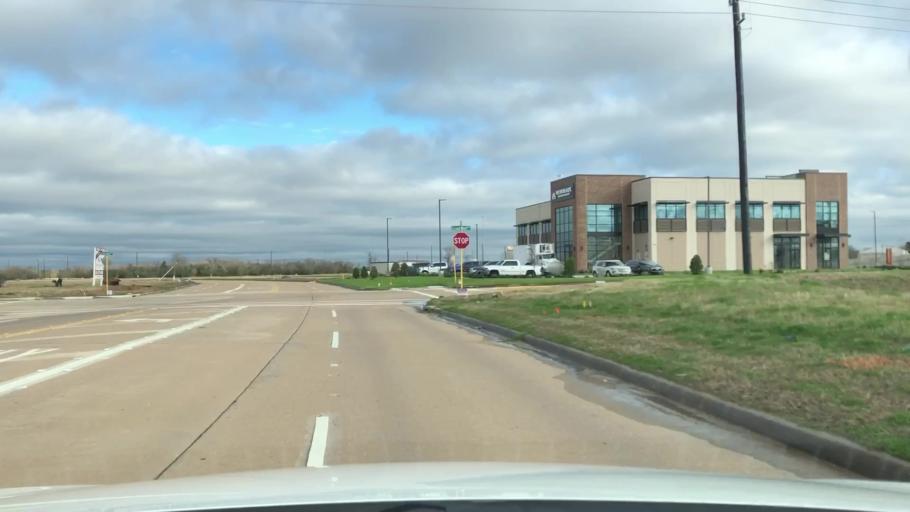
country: US
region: Texas
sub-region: Fort Bend County
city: Cinco Ranch
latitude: 29.7873
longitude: -95.7712
